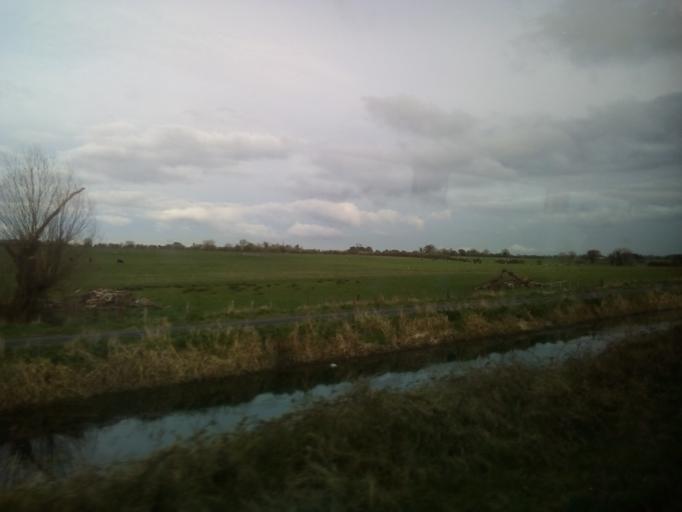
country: IE
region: Leinster
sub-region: Kildare
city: Kilcock
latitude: 53.4162
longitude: -6.6994
